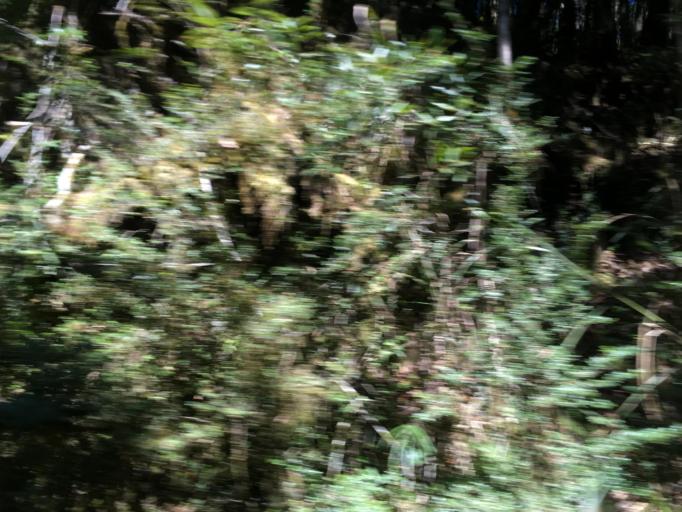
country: TW
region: Taiwan
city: Daxi
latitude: 24.5915
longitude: 121.4198
